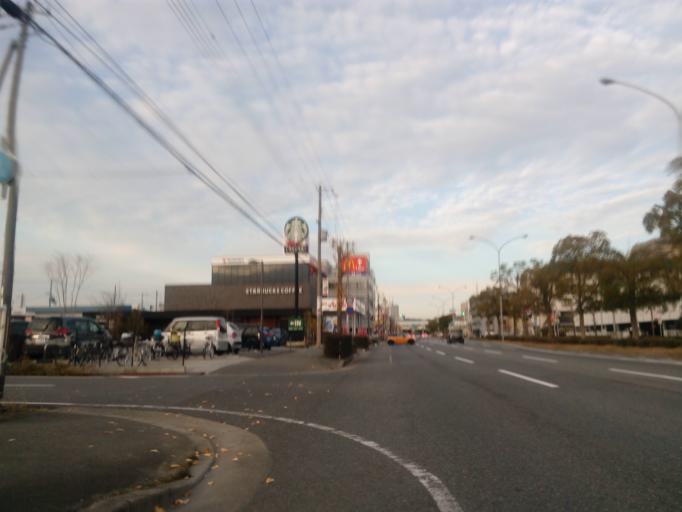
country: JP
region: Hyogo
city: Himeji
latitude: 34.8088
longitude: 134.6809
